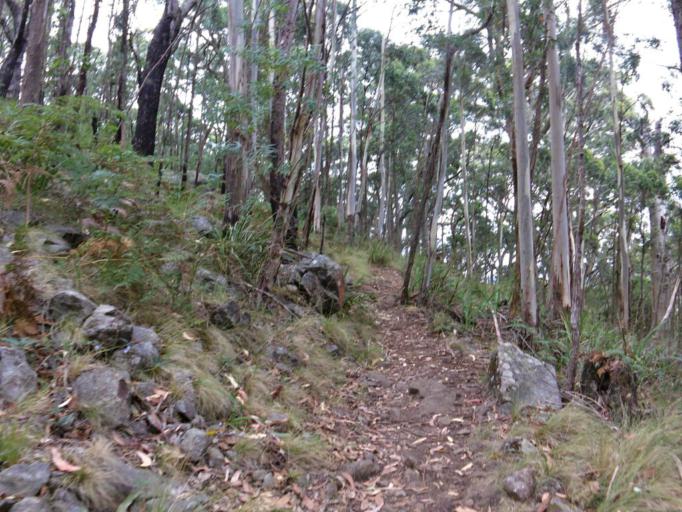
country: AU
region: Victoria
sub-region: Hume
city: Sunbury
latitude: -37.3935
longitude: 144.5748
